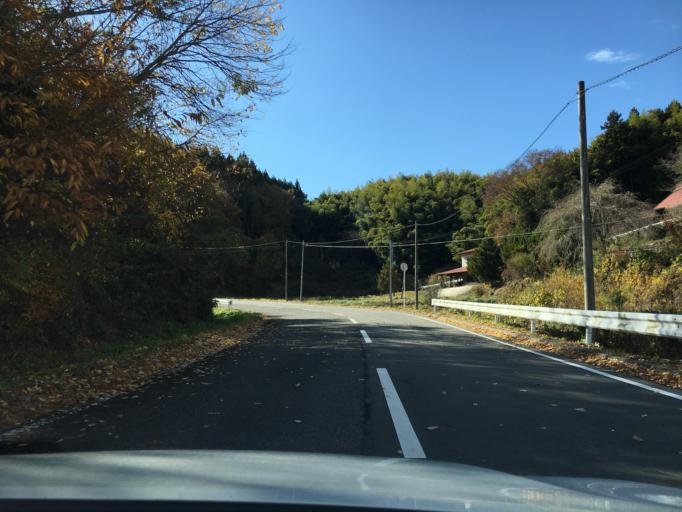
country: JP
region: Fukushima
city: Miharu
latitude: 37.4533
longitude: 140.4562
